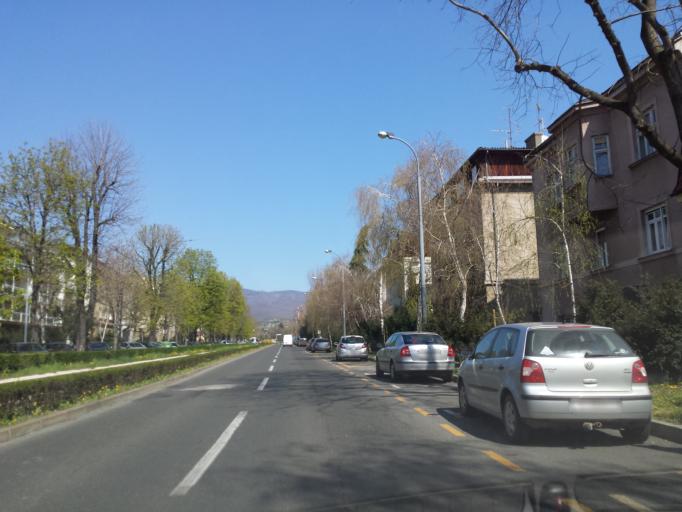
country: HR
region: Grad Zagreb
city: Zagreb
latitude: 45.8253
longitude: 15.9804
